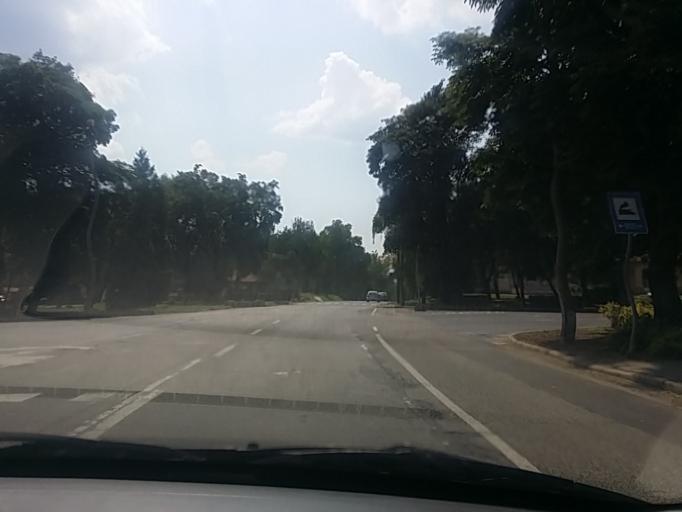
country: HU
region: Tolna
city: Dombovar
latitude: 46.3693
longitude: 18.1294
